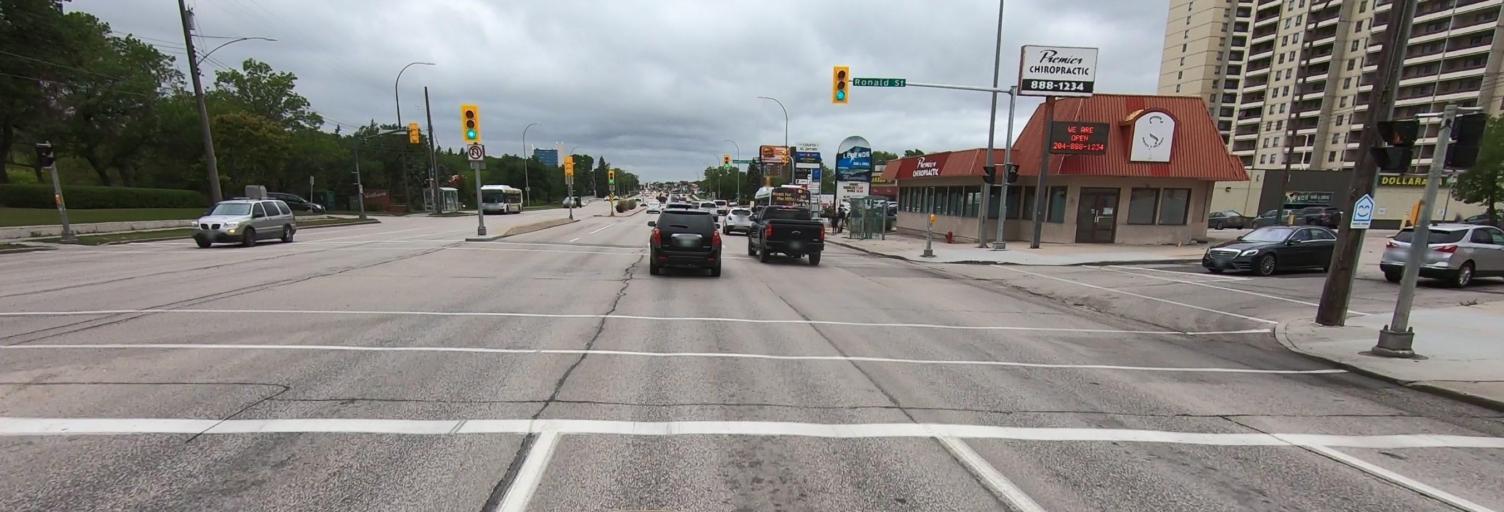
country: CA
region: Manitoba
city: Winnipeg
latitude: 49.8778
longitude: -97.2717
